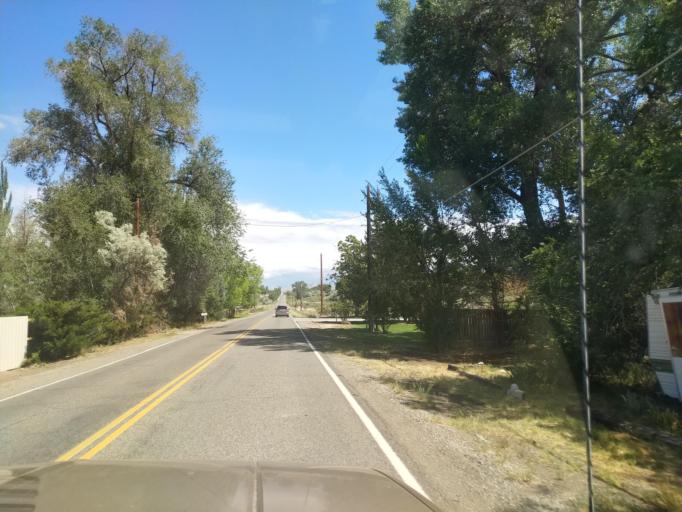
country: US
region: Colorado
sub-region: Mesa County
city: Redlands
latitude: 39.1237
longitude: -108.6081
